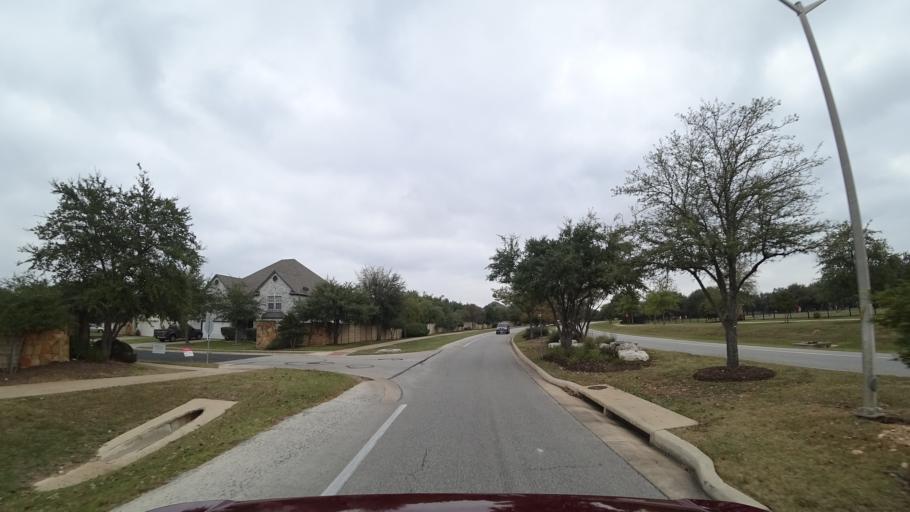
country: US
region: Texas
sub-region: Williamson County
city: Cedar Park
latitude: 30.4825
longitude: -97.8512
